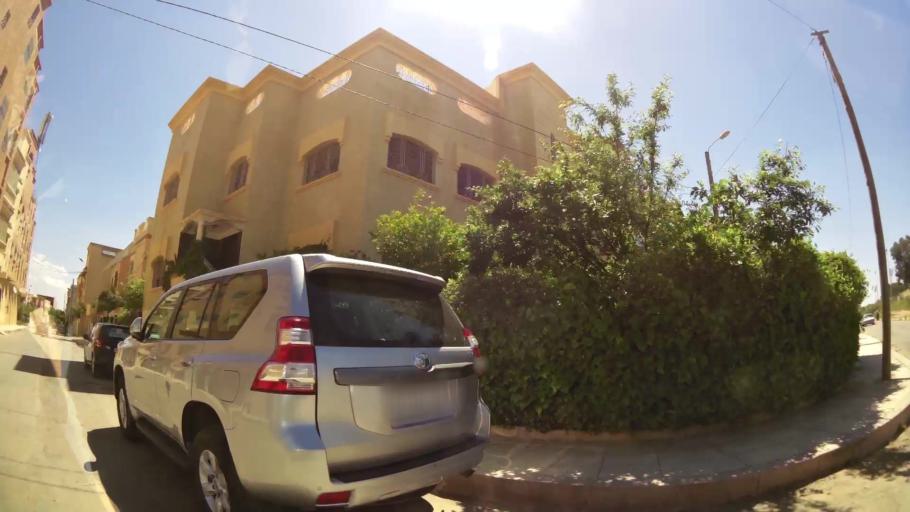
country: MA
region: Oriental
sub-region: Oujda-Angad
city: Oujda
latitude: 34.6641
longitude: -1.9348
